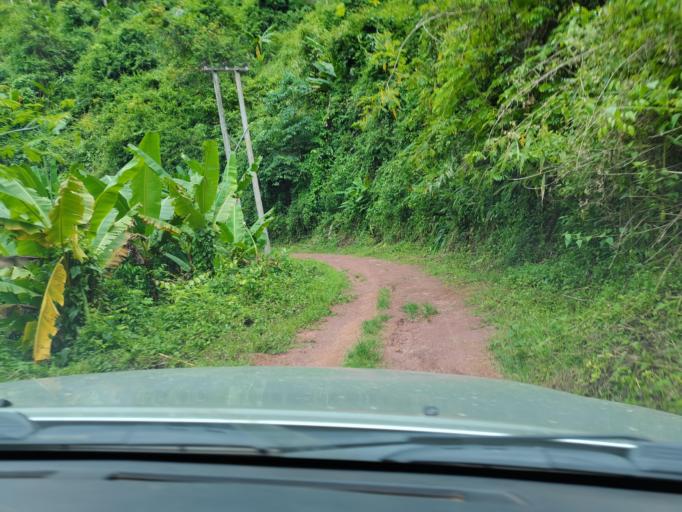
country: LA
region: Loungnamtha
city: Muang Nale
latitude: 20.5157
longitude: 101.0757
